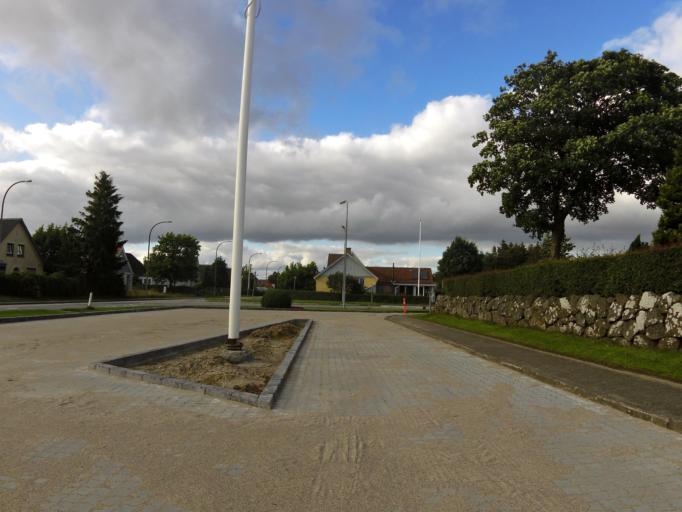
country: DK
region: South Denmark
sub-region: Tonder Kommune
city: Toftlund
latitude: 55.1826
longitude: 9.0662
